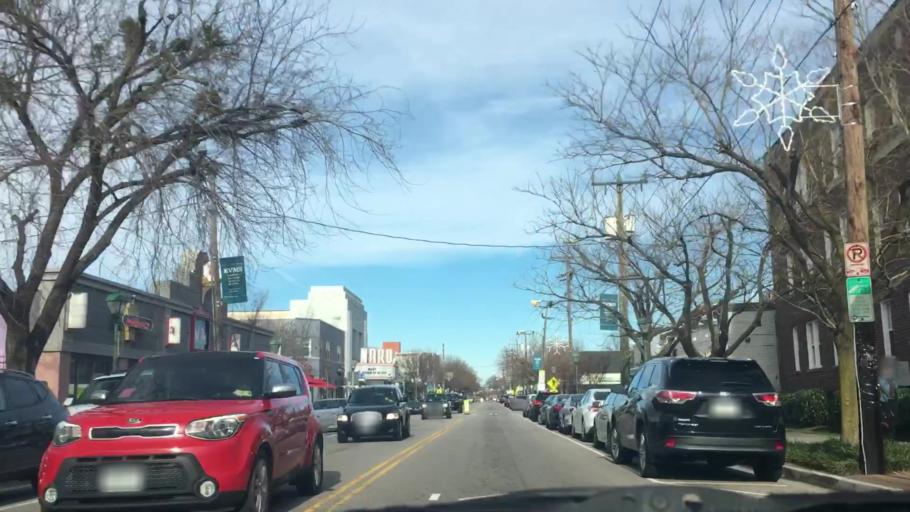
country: US
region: Virginia
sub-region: City of Norfolk
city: Norfolk
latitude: 36.8673
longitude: -76.2982
